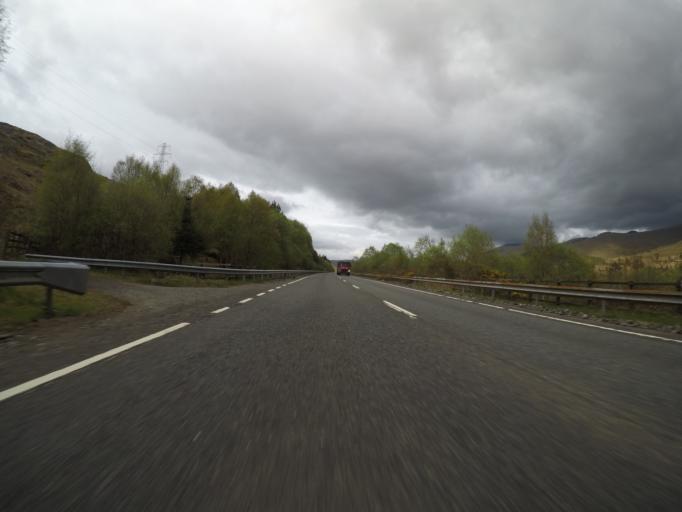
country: GB
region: Scotland
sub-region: Argyll and Bute
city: Garelochhead
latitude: 56.3706
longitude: -4.6575
